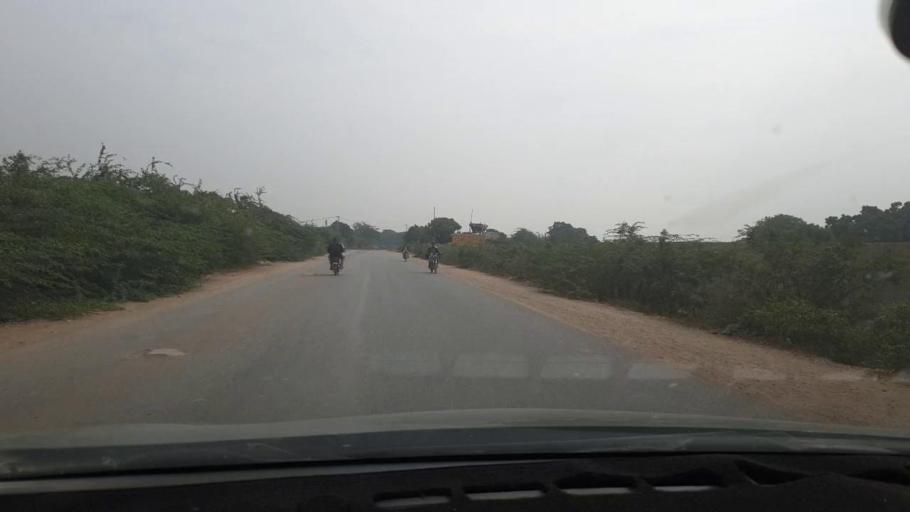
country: PK
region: Sindh
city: Malir Cantonment
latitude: 24.9160
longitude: 67.2604
